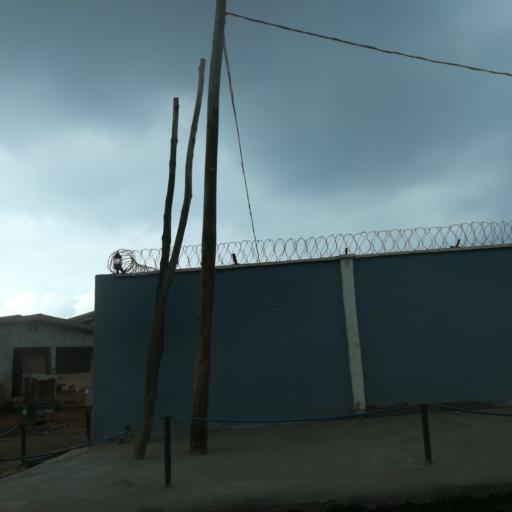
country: NG
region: Lagos
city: Agege
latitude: 6.5924
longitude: 3.3047
